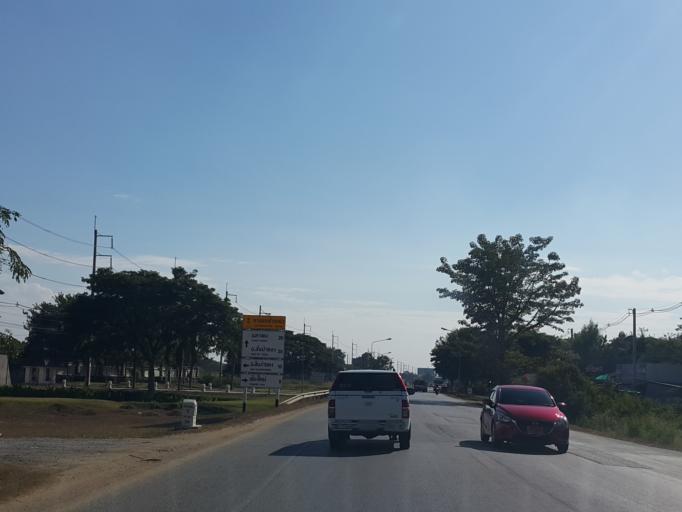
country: TH
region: Chiang Mai
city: San Kamphaeng
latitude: 18.7777
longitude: 99.0695
